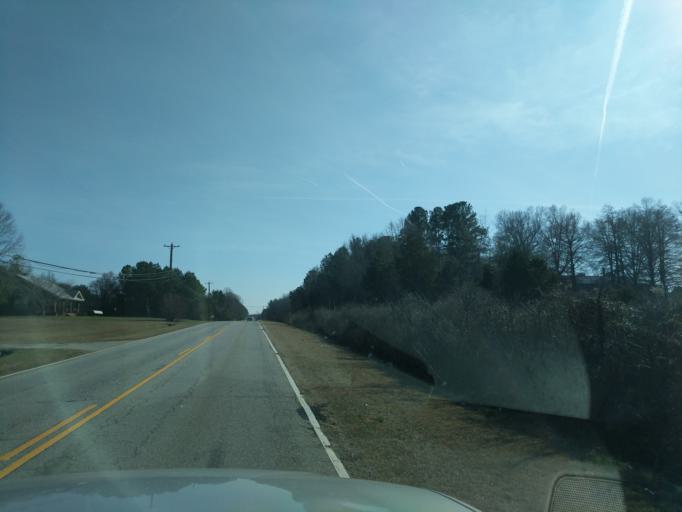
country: US
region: South Carolina
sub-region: Spartanburg County
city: Woodruff
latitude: 34.7137
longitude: -82.0204
